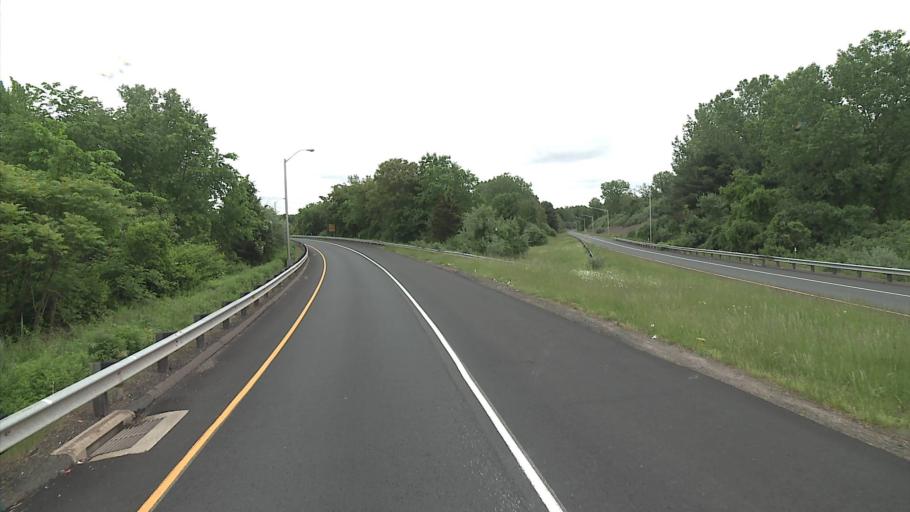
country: US
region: Connecticut
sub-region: Middlesex County
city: Cromwell
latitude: 41.6198
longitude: -72.6931
